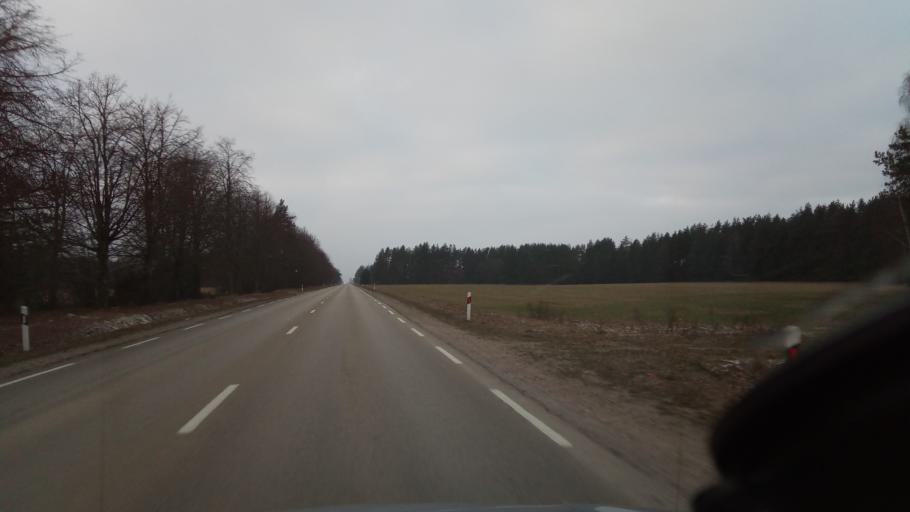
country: LT
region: Alytaus apskritis
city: Varena
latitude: 54.3465
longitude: 24.5923
